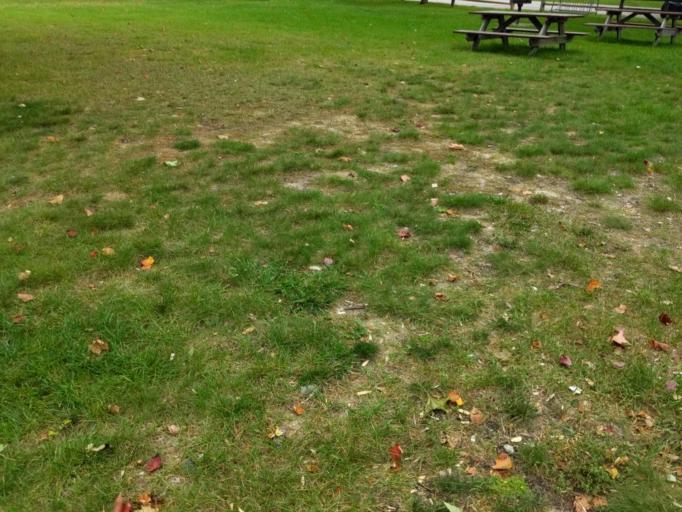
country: US
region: Michigan
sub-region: Kalkaska County
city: Rapid City
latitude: 44.8825
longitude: -85.2740
